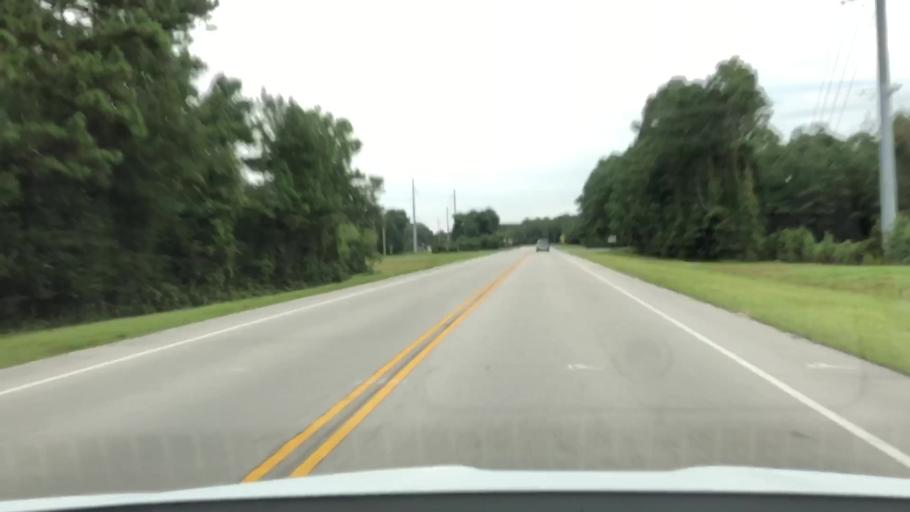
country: US
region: North Carolina
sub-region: Carteret County
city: Cape Carteret
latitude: 34.6972
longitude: -77.0692
